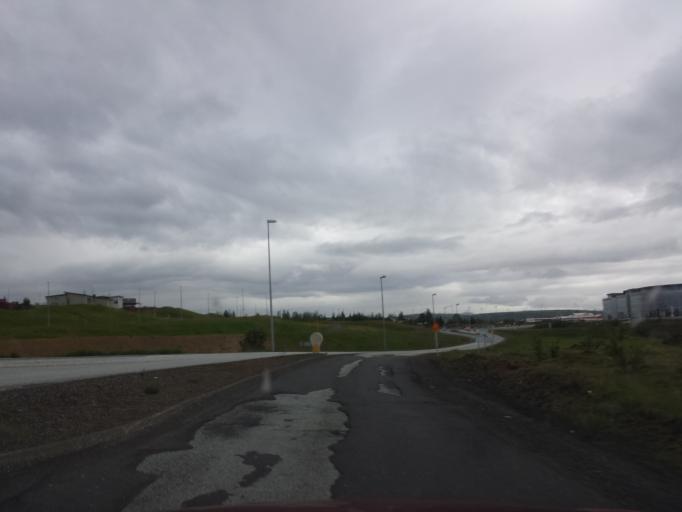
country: IS
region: Capital Region
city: Hafnarfjoerdur
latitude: 64.0848
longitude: -21.9512
